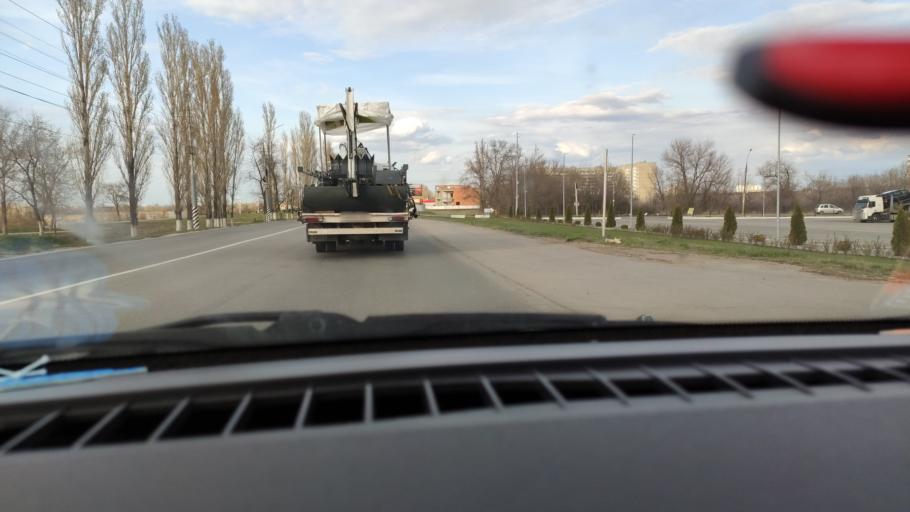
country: RU
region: Saratov
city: Privolzhskiy
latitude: 51.4454
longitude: 46.0745
